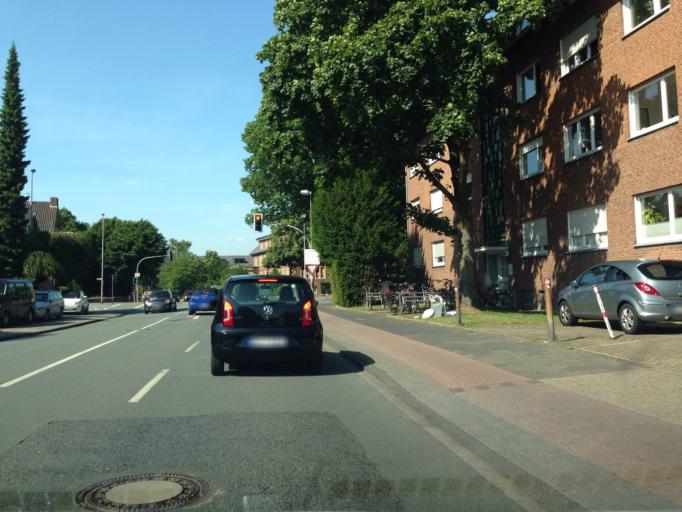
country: DE
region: North Rhine-Westphalia
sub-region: Regierungsbezirk Munster
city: Muenster
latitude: 51.9741
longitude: 7.6234
